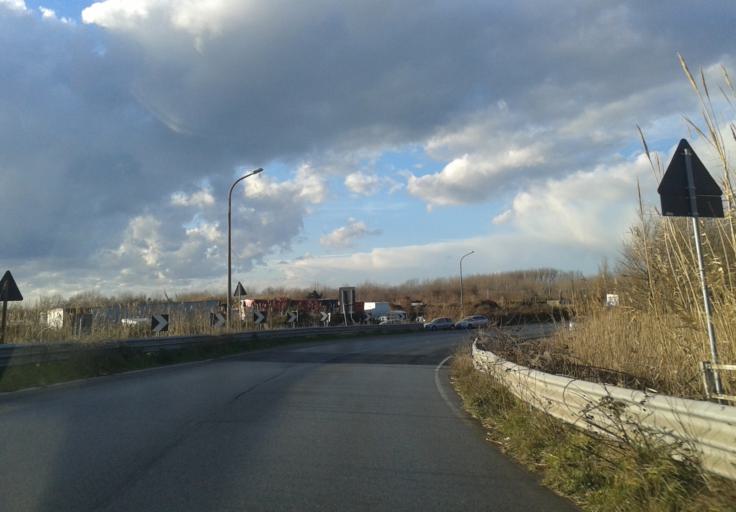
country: IT
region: Tuscany
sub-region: Province of Pisa
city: Marina di Pisa-Tirrenia-Calambrone
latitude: 43.5843
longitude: 10.3017
